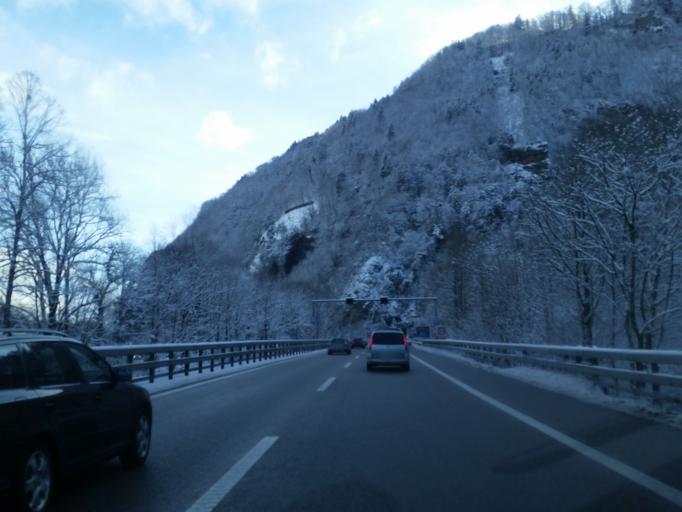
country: CH
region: Saint Gallen
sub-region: Wahlkreis See-Gaster
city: Weesen
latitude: 47.1259
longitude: 9.1107
